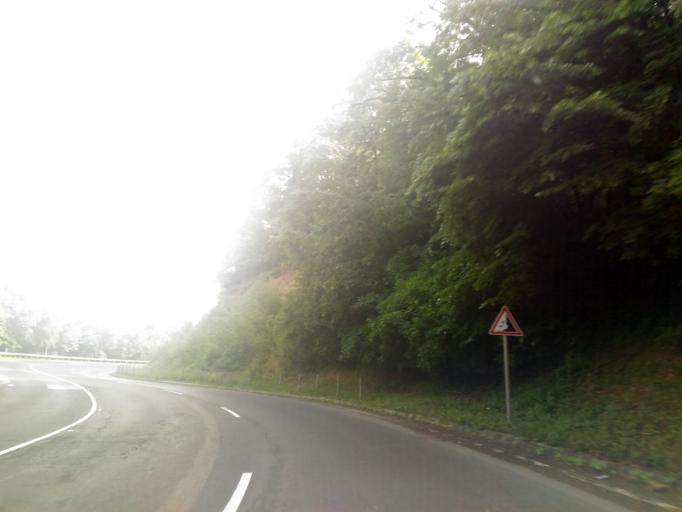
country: HU
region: Baranya
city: Komlo
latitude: 46.1465
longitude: 18.2448
